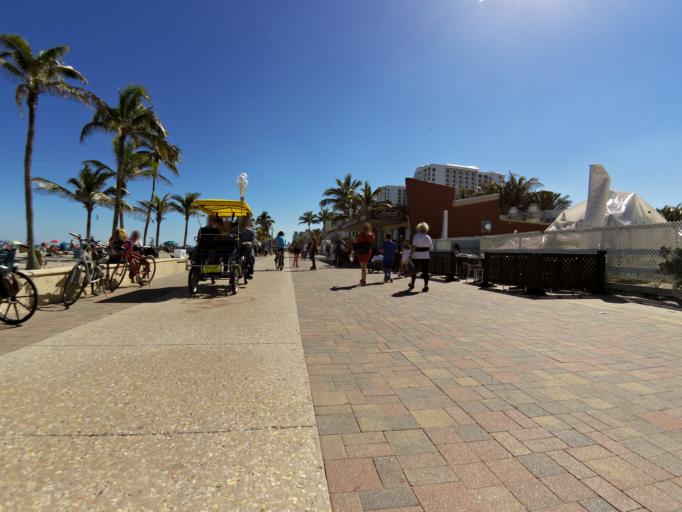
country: US
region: Florida
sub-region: Broward County
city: Hollywood
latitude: 26.0211
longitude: -80.1151
